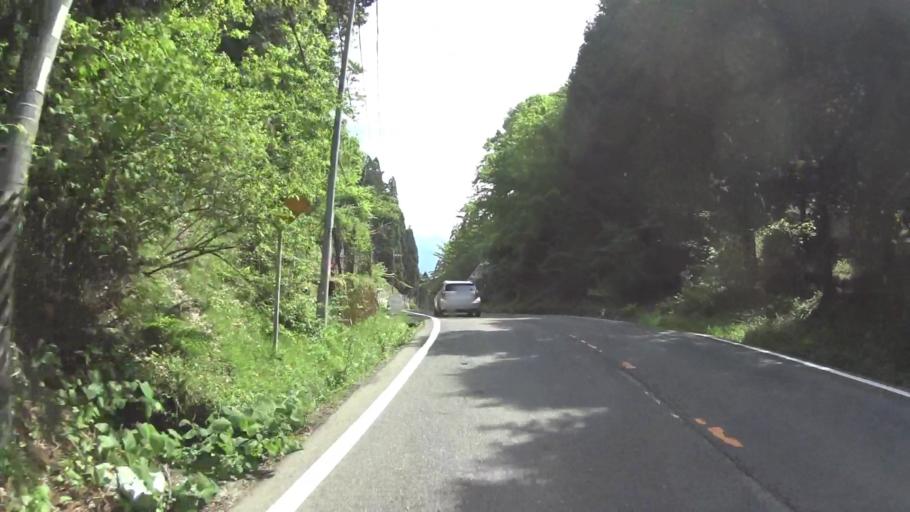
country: JP
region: Fukui
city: Obama
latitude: 35.3881
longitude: 135.9264
